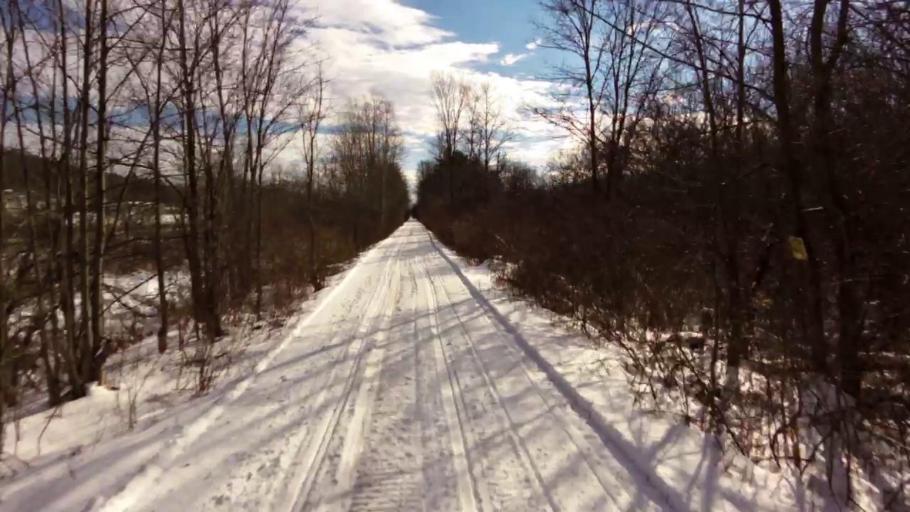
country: US
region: Pennsylvania
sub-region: McKean County
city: Foster Brook
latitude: 42.0453
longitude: -78.6351
